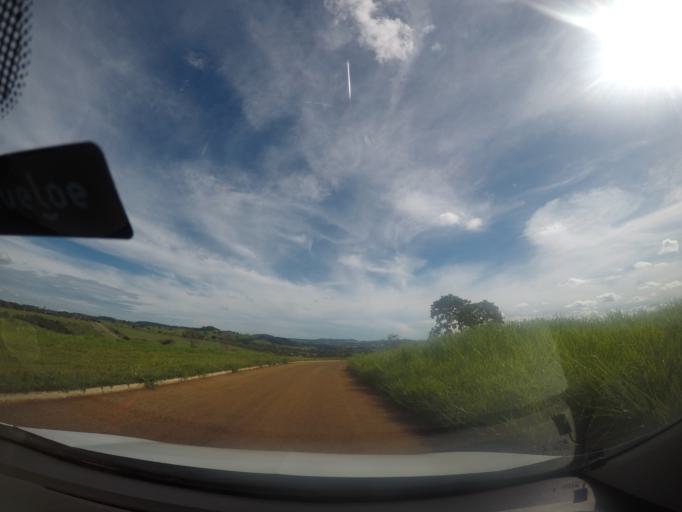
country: BR
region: Goias
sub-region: Inhumas
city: Inhumas
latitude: -16.4110
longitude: -49.4731
